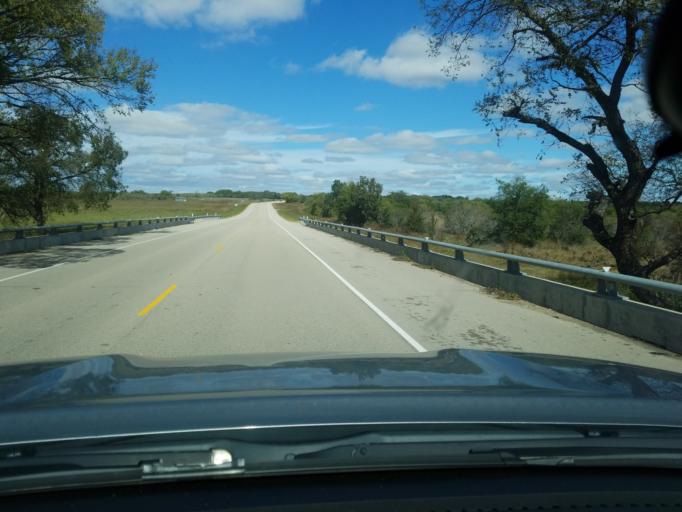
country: US
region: Texas
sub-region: Hamilton County
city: Hamilton
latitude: 31.6083
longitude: -98.1587
